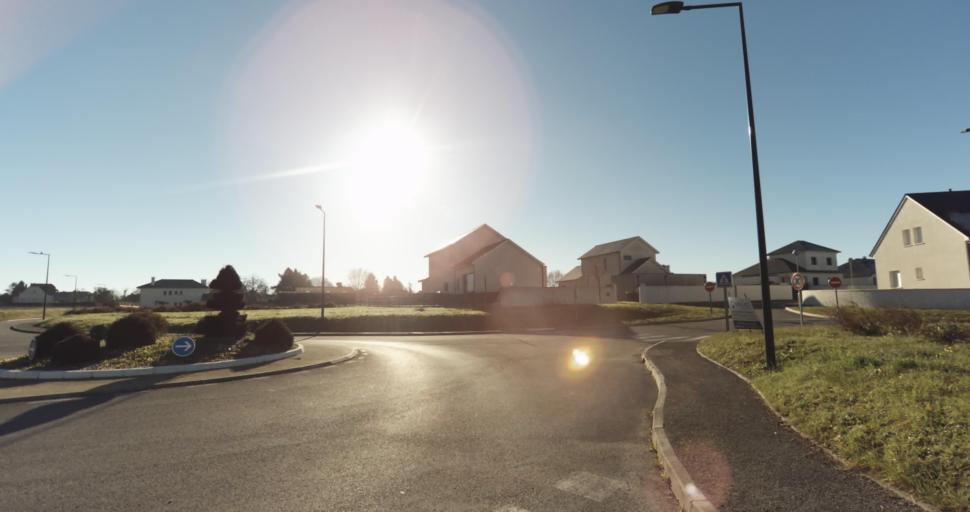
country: FR
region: Aquitaine
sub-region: Departement des Pyrenees-Atlantiques
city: Morlaas
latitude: 43.3409
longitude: -0.2560
